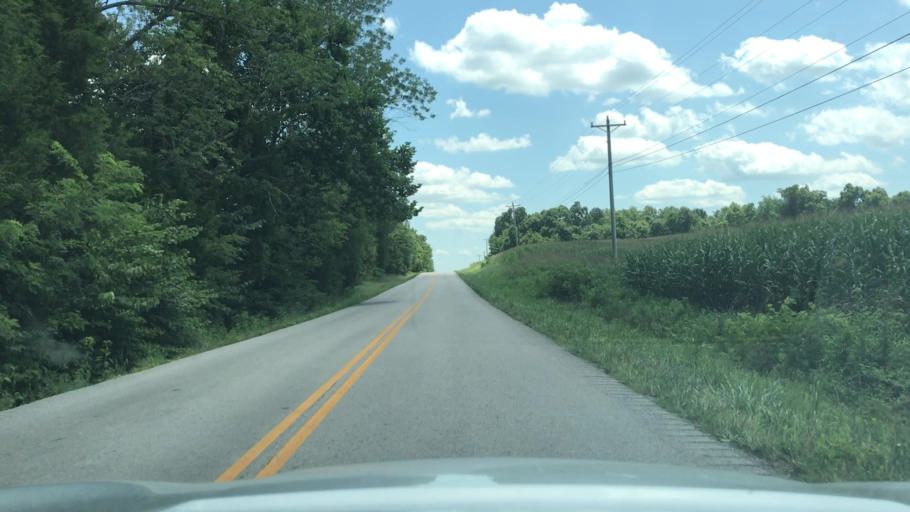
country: US
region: Kentucky
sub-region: Christian County
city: Hopkinsville
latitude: 36.9930
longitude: -87.3630
